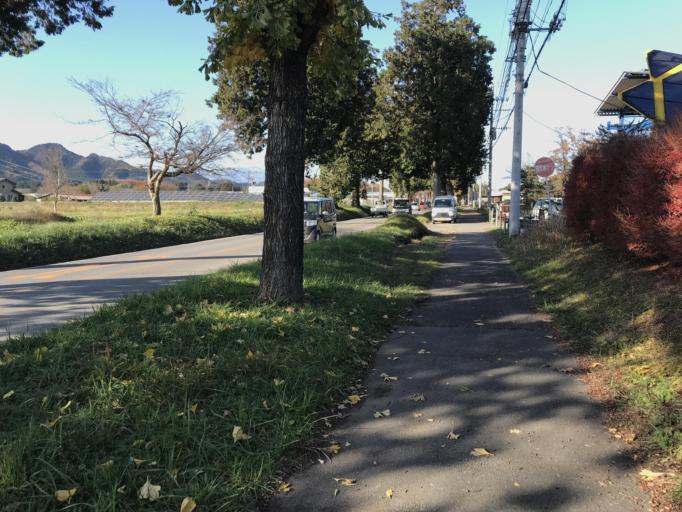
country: JP
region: Tochigi
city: Kanuma
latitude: 36.6036
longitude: 139.7426
